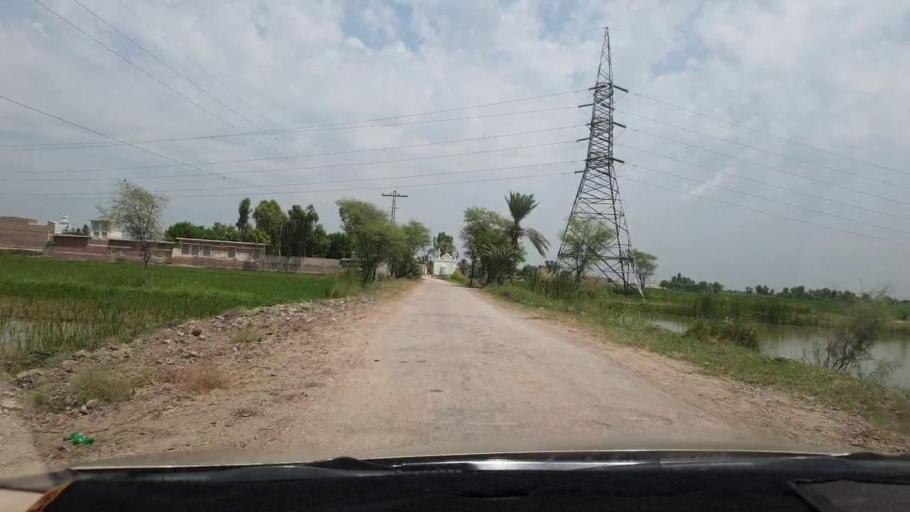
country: PK
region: Sindh
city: Naudero
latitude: 27.7229
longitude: 68.3363
